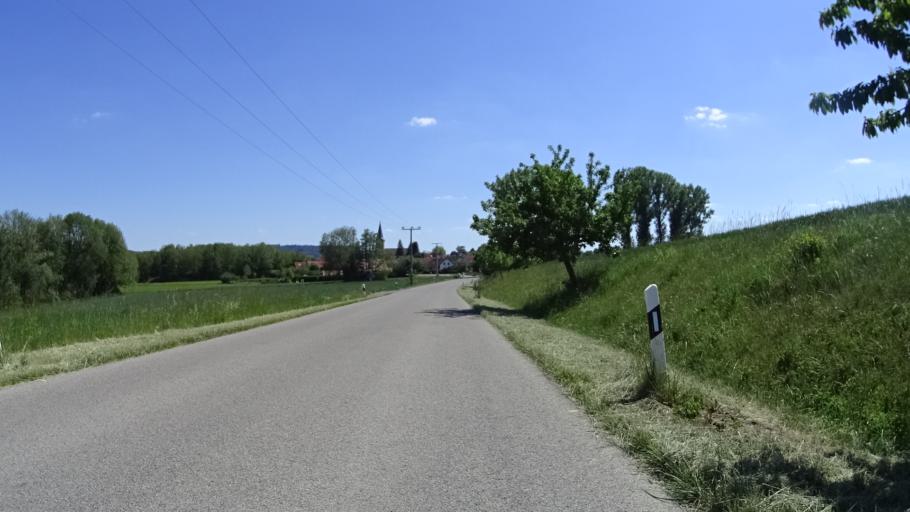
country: DE
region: Bavaria
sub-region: Regierungsbezirk Mittelfranken
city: Gebsattel
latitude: 49.3554
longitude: 10.1938
